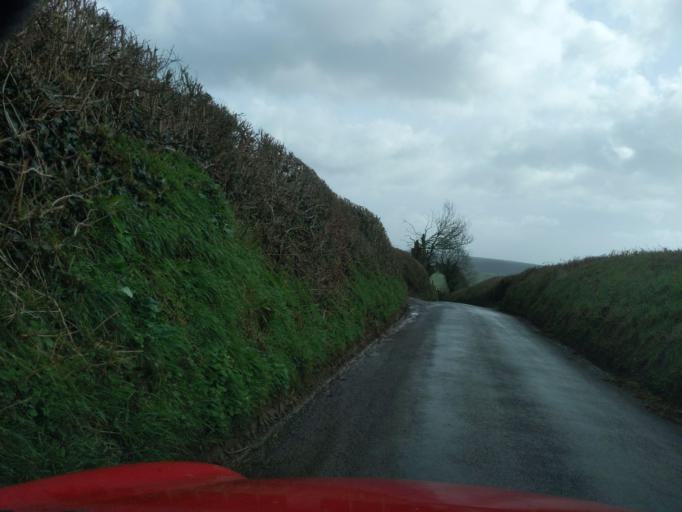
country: GB
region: England
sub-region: Devon
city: Ivybridge
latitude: 50.3646
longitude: -3.9320
